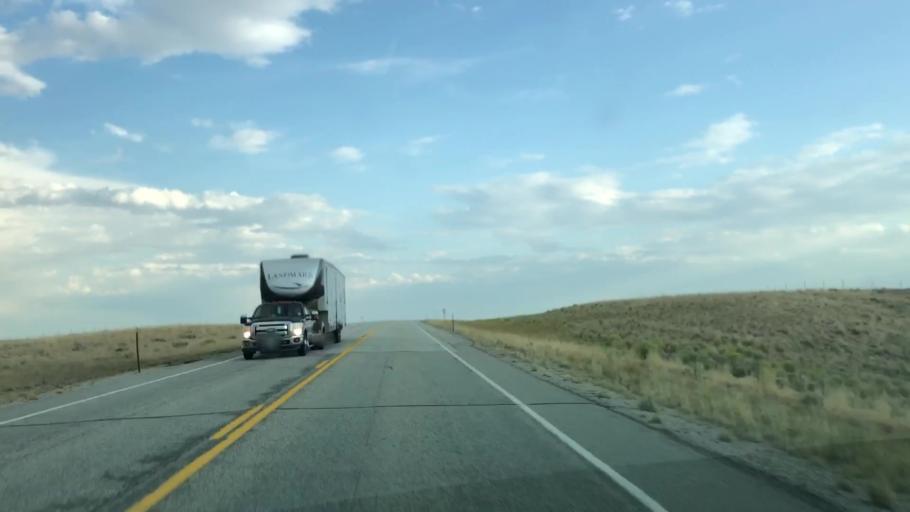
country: US
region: Wyoming
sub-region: Sweetwater County
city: North Rock Springs
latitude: 42.2781
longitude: -109.4841
